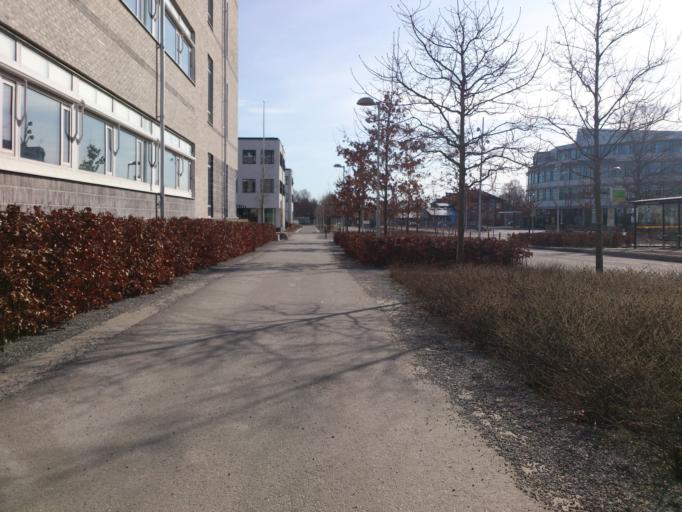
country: SE
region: Uppsala
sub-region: Uppsala Kommun
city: Saevja
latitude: 59.8166
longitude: 17.6599
